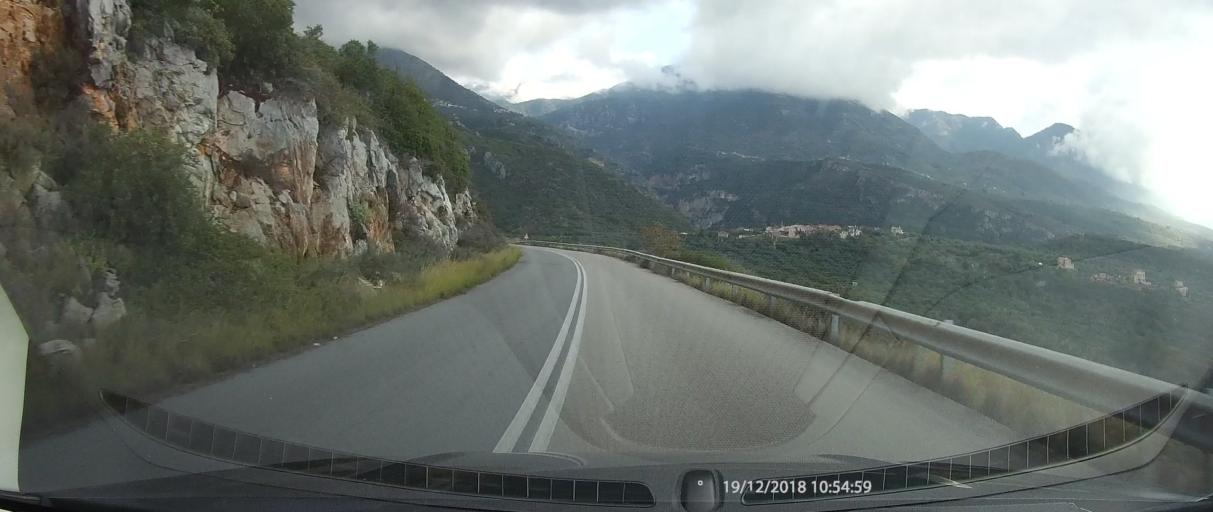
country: GR
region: Peloponnese
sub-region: Nomos Messinias
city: Kardamyli
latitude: 36.9047
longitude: 22.2378
